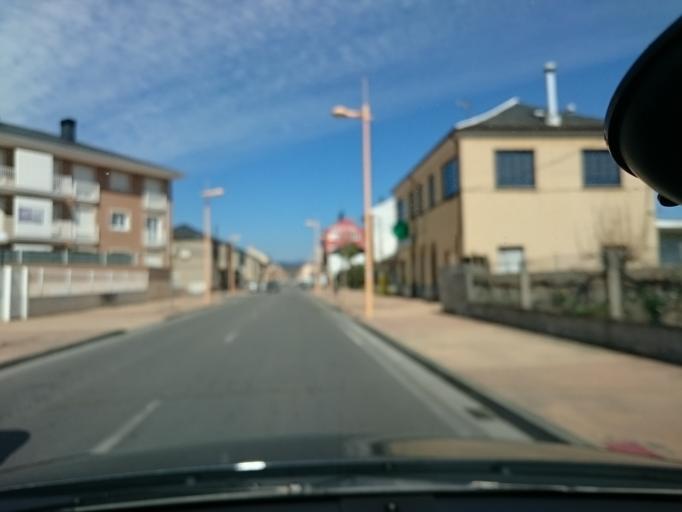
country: ES
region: Castille and Leon
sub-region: Provincia de Leon
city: Camponaraya
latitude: 42.5667
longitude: -6.6392
